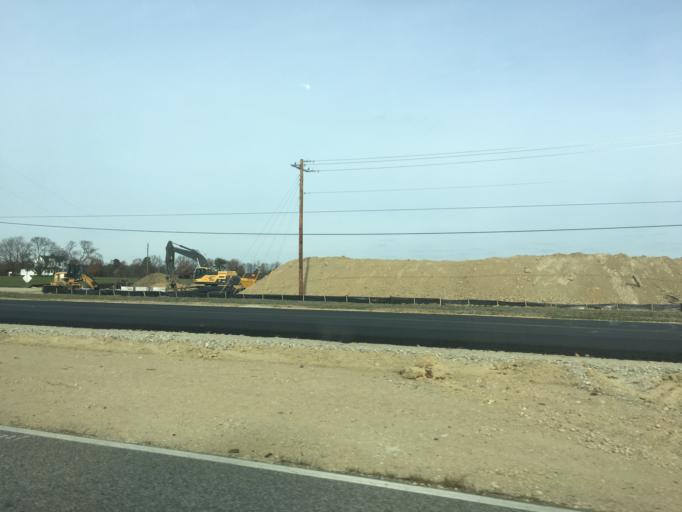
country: US
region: Maryland
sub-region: Queen Anne's County
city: Centreville
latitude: 38.9300
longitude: -76.0119
